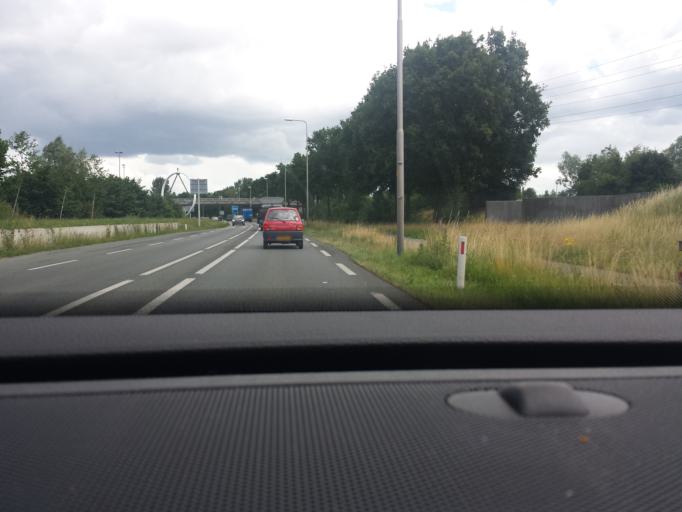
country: NL
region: Gelderland
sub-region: Gemeente Zutphen
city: Leesten
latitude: 52.1306
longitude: 6.2190
